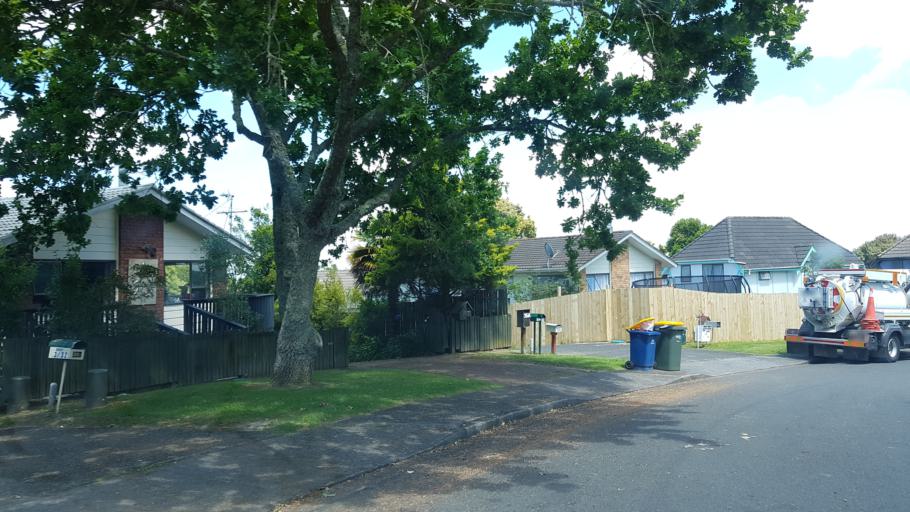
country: NZ
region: Auckland
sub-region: Auckland
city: North Shore
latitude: -36.7893
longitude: 174.7084
